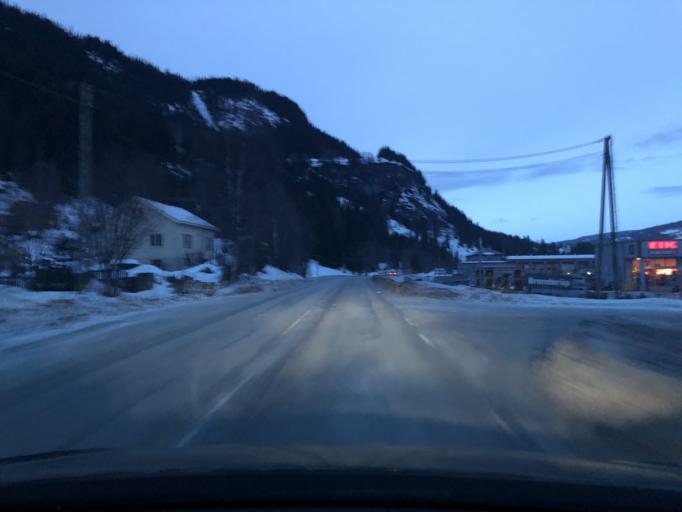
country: NO
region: Oppland
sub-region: Nord-Aurdal
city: Fagernes
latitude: 60.9960
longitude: 9.2143
